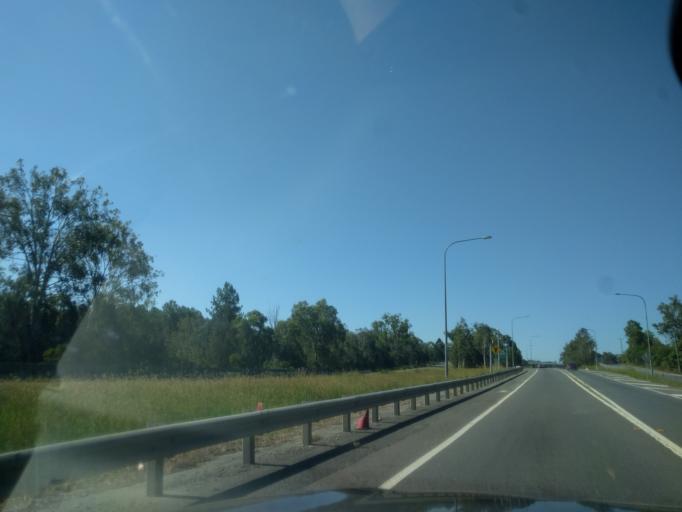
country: AU
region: Queensland
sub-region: Logan
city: Park Ridge South
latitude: -27.7299
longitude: 153.0292
